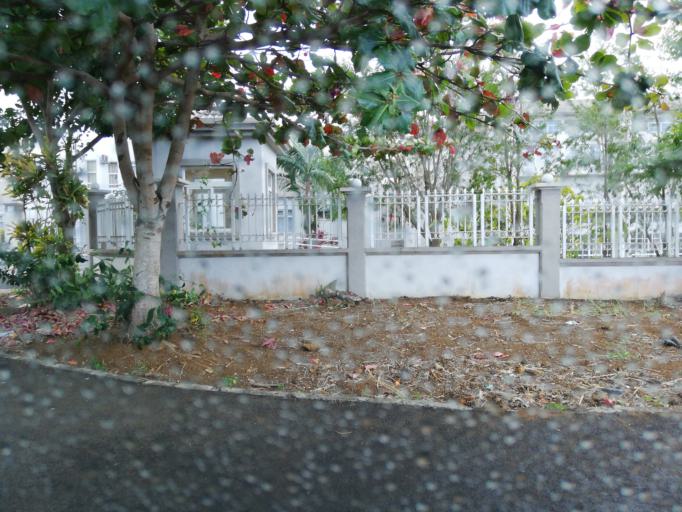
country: MU
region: Plaines Wilhems
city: Ebene
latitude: -20.2463
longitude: 57.4828
